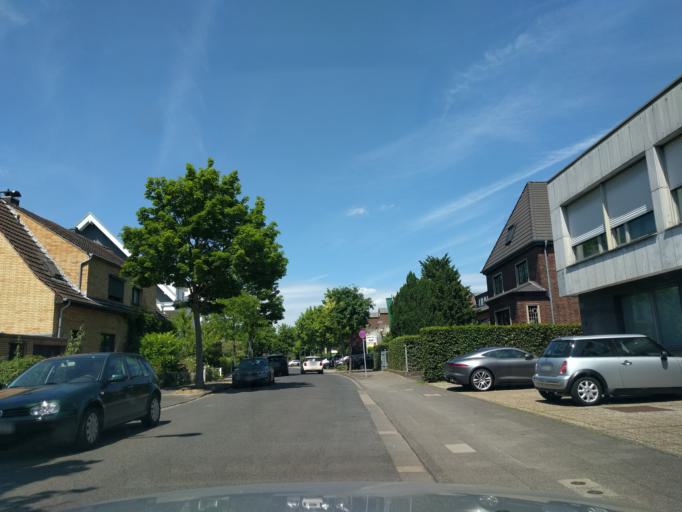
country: DE
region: North Rhine-Westphalia
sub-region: Regierungsbezirk Dusseldorf
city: Meerbusch
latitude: 51.2487
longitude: 6.7044
